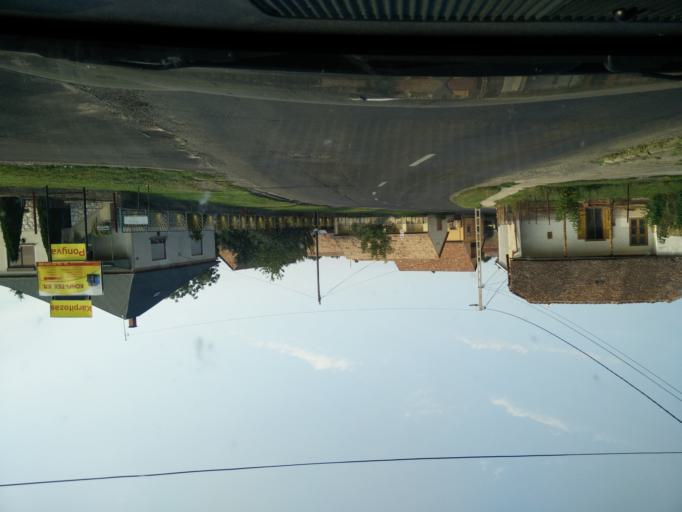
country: HU
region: Baranya
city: Szaszvar
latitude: 46.2765
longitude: 18.3769
